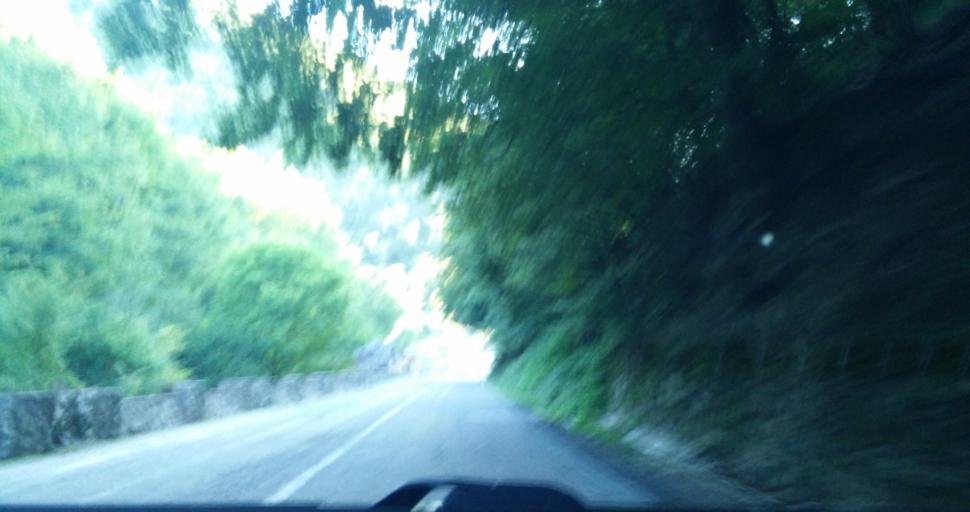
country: RO
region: Bihor
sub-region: Oras Nucet
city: Nucet
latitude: 46.4829
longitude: 22.5959
